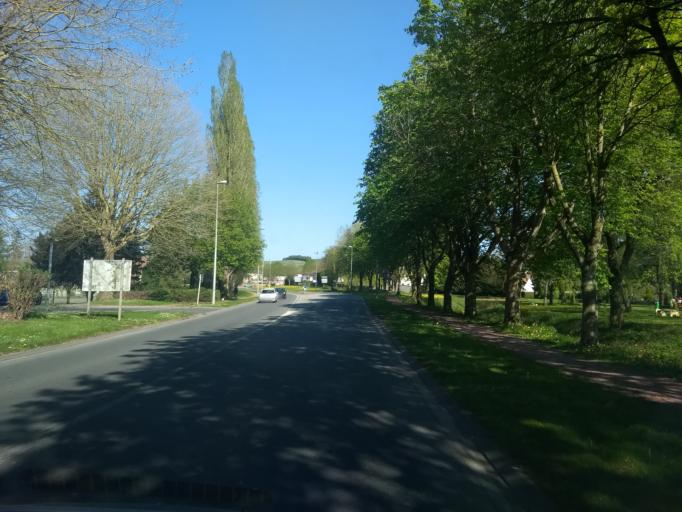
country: FR
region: Picardie
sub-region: Departement de la Somme
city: Doullens
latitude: 50.1539
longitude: 2.3447
